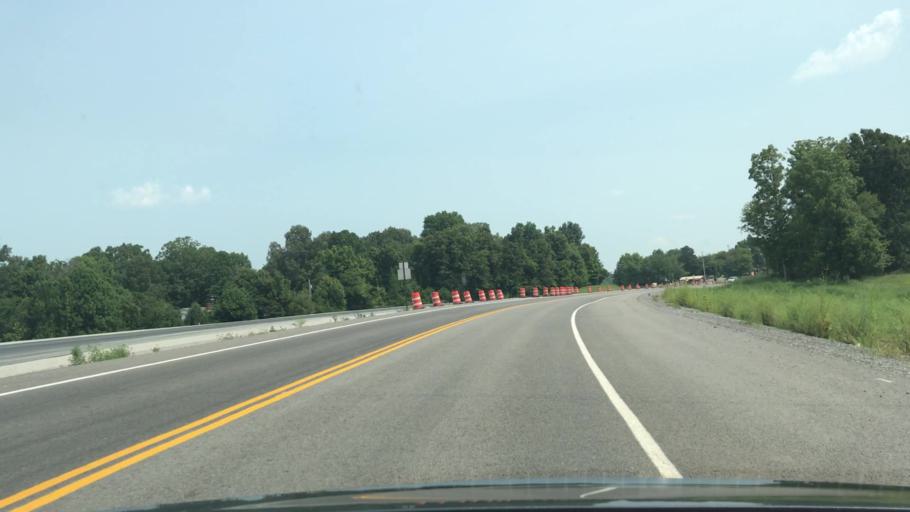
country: US
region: Kentucky
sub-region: Trigg County
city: Cadiz
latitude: 36.8370
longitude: -87.8628
